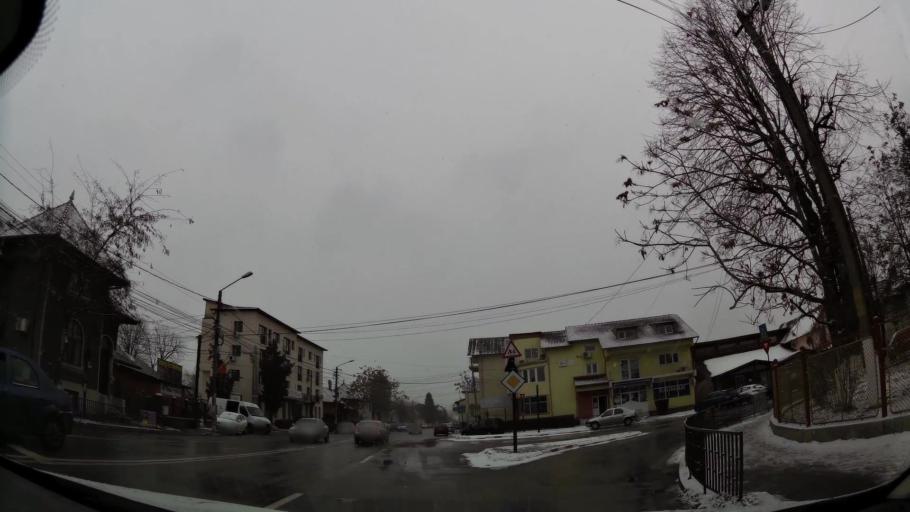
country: RO
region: Dambovita
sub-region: Municipiul Targoviste
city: Targoviste
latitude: 44.9265
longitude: 25.4679
